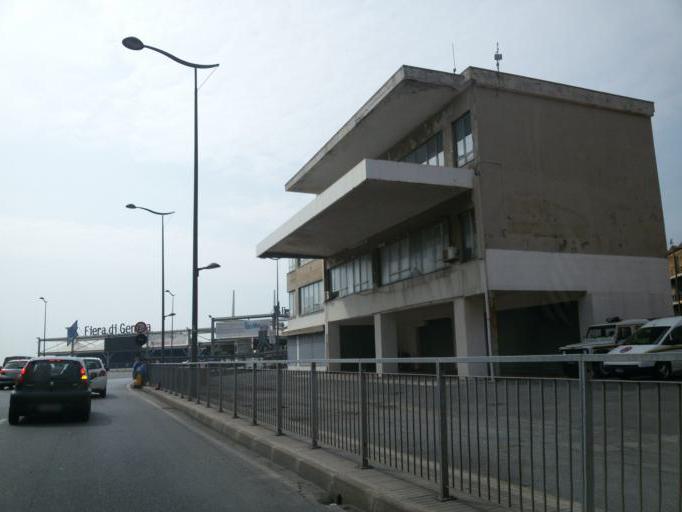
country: IT
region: Liguria
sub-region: Provincia di Genova
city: San Teodoro
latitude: 44.3971
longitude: 8.9436
